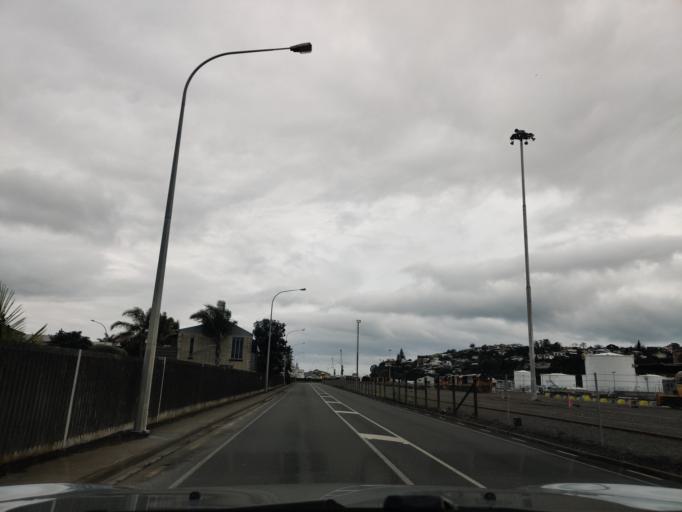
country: NZ
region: Hawke's Bay
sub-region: Napier City
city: Napier
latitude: -39.4812
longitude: 176.8990
